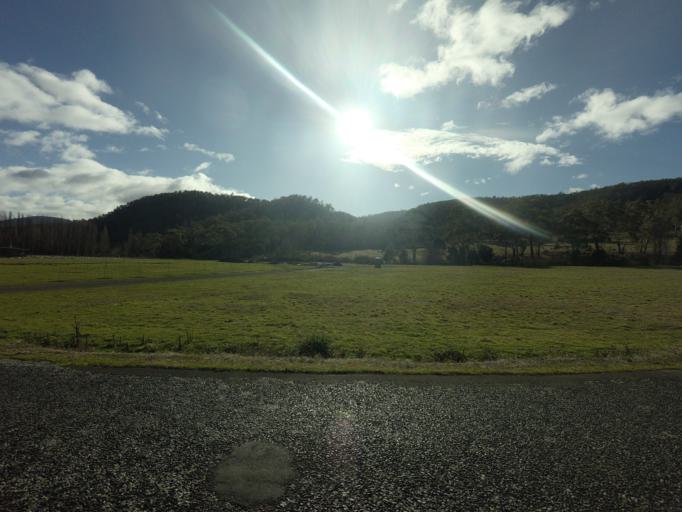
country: AU
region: Tasmania
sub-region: Derwent Valley
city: New Norfolk
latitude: -42.8007
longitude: 147.1417
